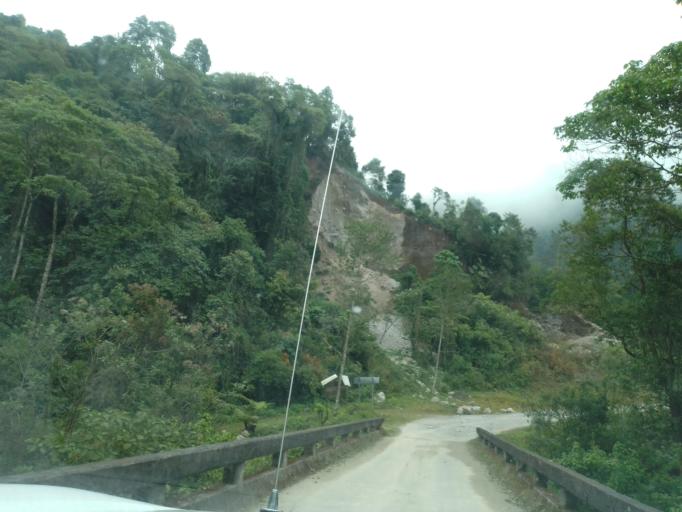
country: MX
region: Chiapas
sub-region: Union Juarez
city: Santo Domingo
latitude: 15.0929
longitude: -92.0939
